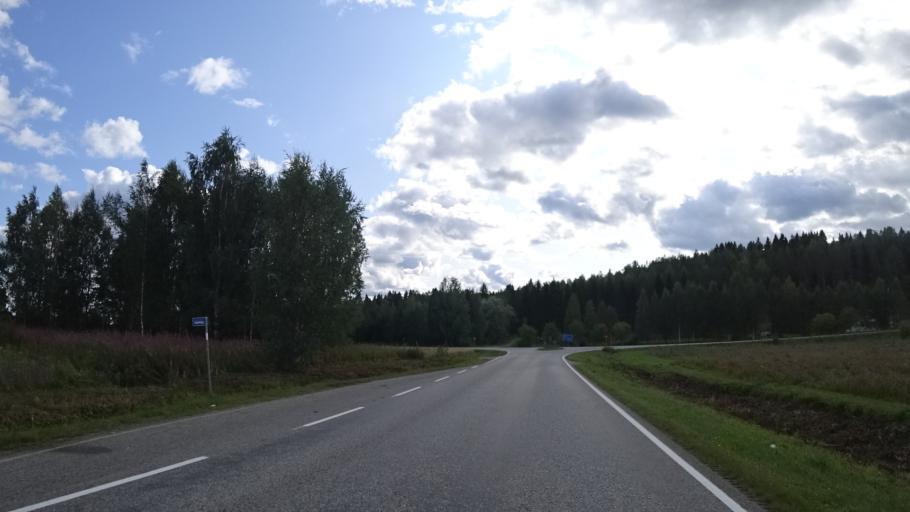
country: RU
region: Republic of Karelia
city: Vyartsilya
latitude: 62.2140
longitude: 30.6006
